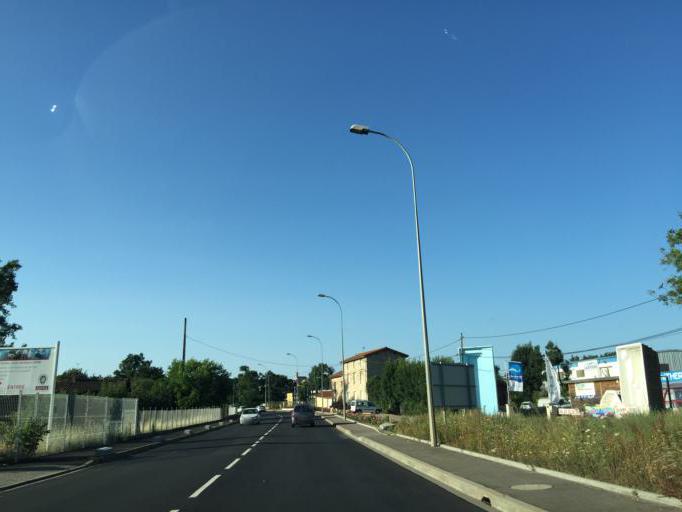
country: FR
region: Rhone-Alpes
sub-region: Departement de la Loire
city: La Talaudiere
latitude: 45.4751
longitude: 4.4426
